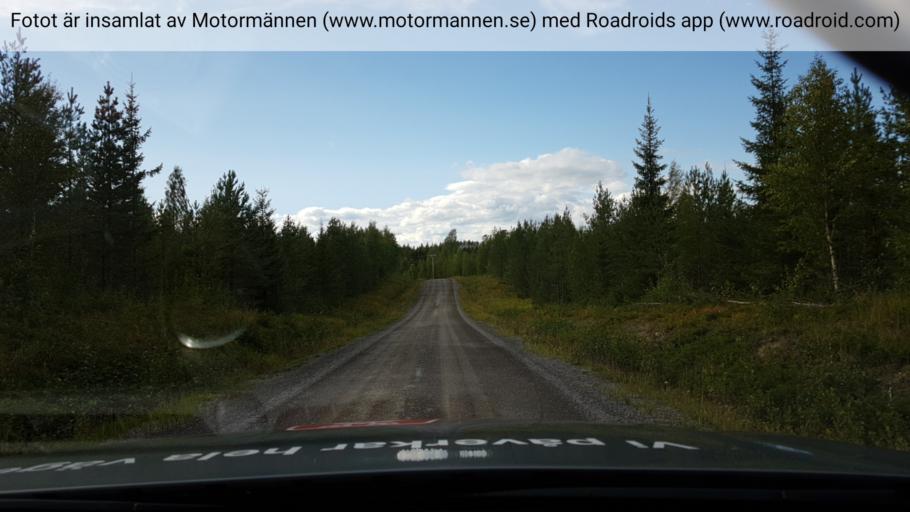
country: SE
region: Jaemtland
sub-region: OEstersunds Kommun
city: Lit
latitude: 63.2997
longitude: 15.3182
